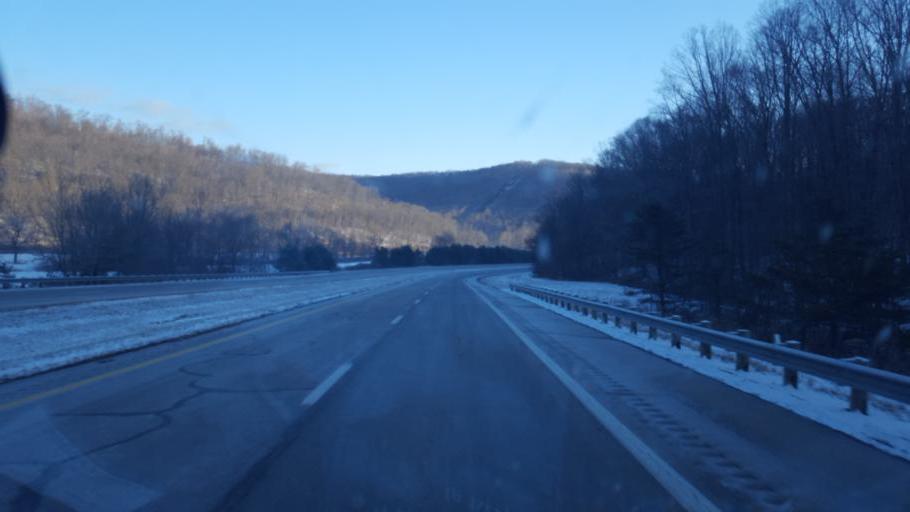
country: US
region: Ohio
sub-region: Adams County
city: Peebles
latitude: 39.0348
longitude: -83.2594
